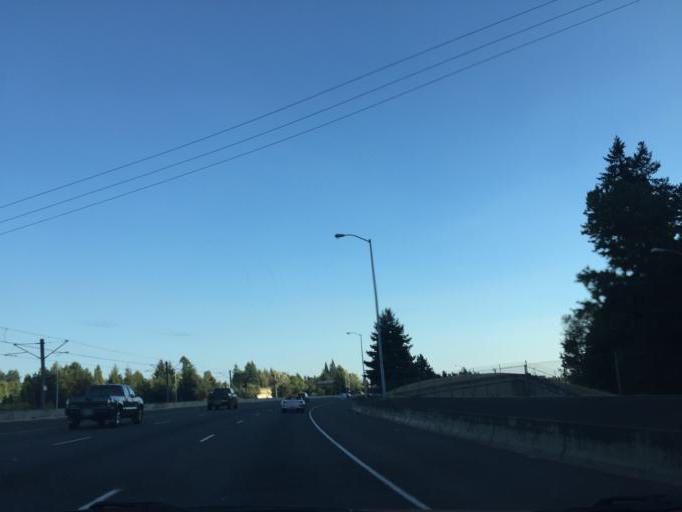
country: US
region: Oregon
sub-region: Multnomah County
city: Lents
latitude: 45.5490
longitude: -122.5615
